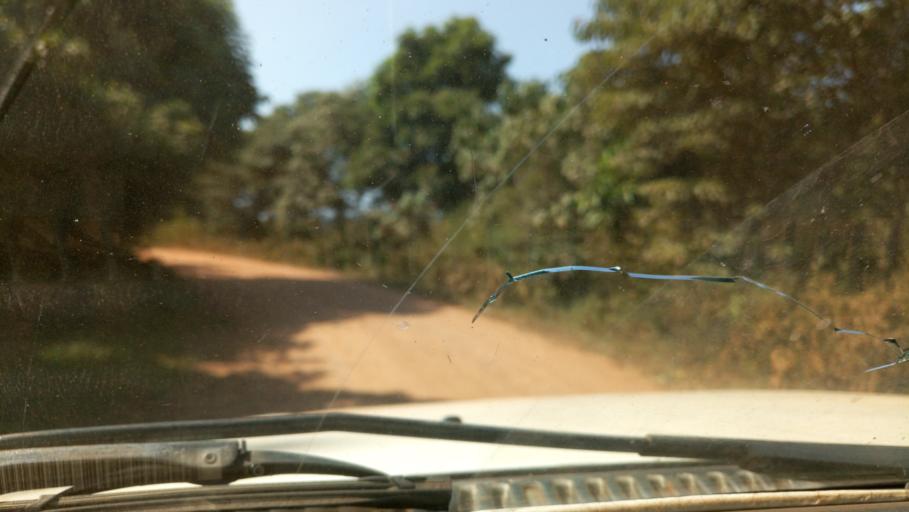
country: KE
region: Kirinyaga
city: Sagana
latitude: -0.6475
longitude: 37.1672
